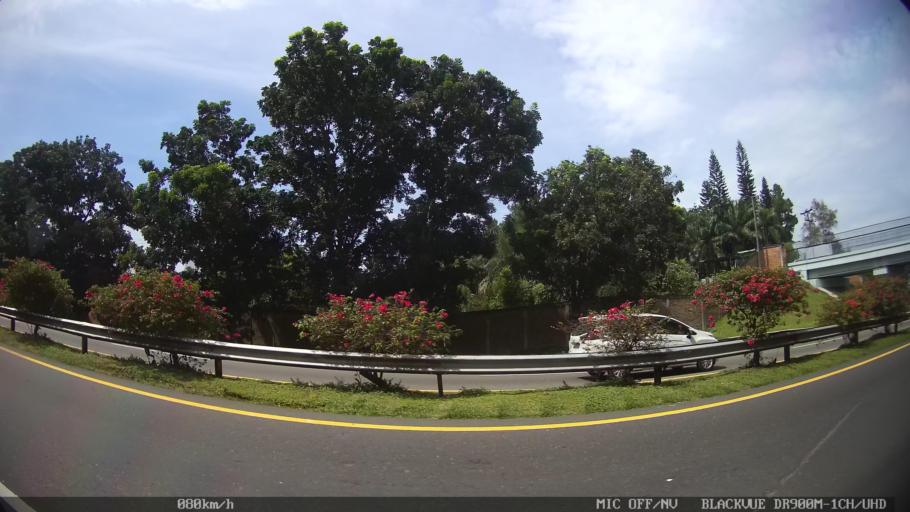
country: ID
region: North Sumatra
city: Medan
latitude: 3.6419
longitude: 98.6958
